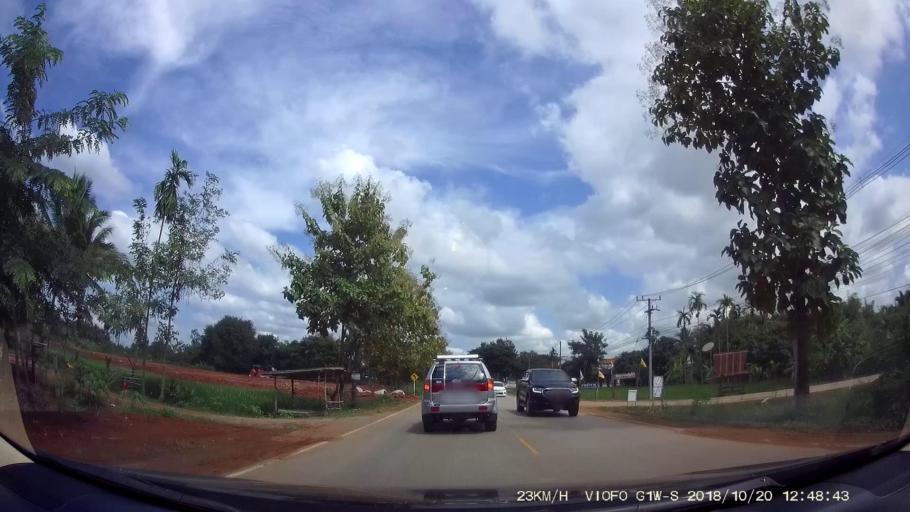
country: TH
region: Chaiyaphum
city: Khon San
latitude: 16.5368
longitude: 101.8939
